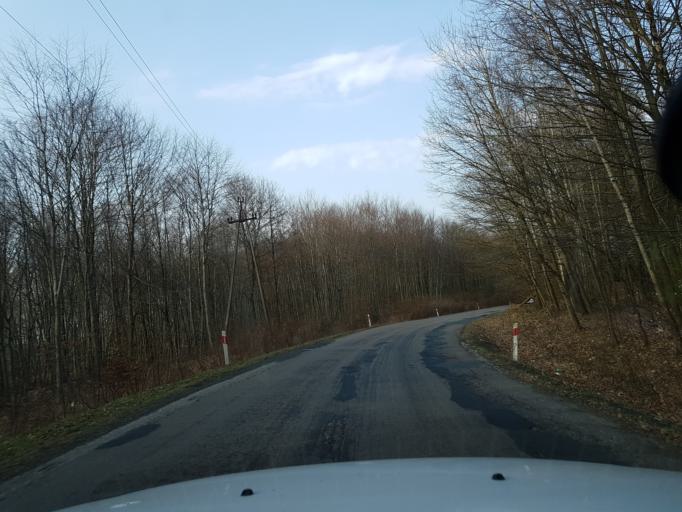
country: PL
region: West Pomeranian Voivodeship
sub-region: Powiat swidwinski
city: Polczyn-Zdroj
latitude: 53.7355
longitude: 16.0759
